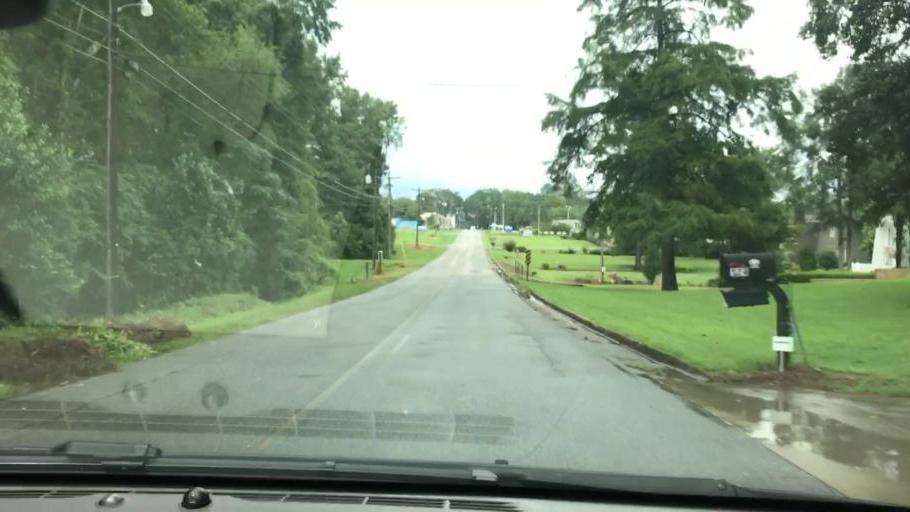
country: US
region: Georgia
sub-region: Early County
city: Blakely
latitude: 31.3695
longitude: -84.9470
